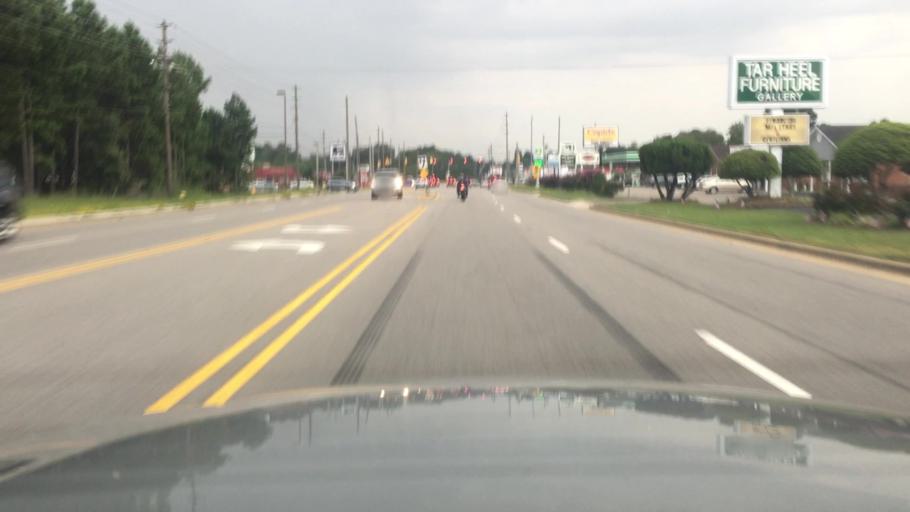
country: US
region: North Carolina
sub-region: Cumberland County
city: Fort Bragg
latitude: 35.0846
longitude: -79.0104
